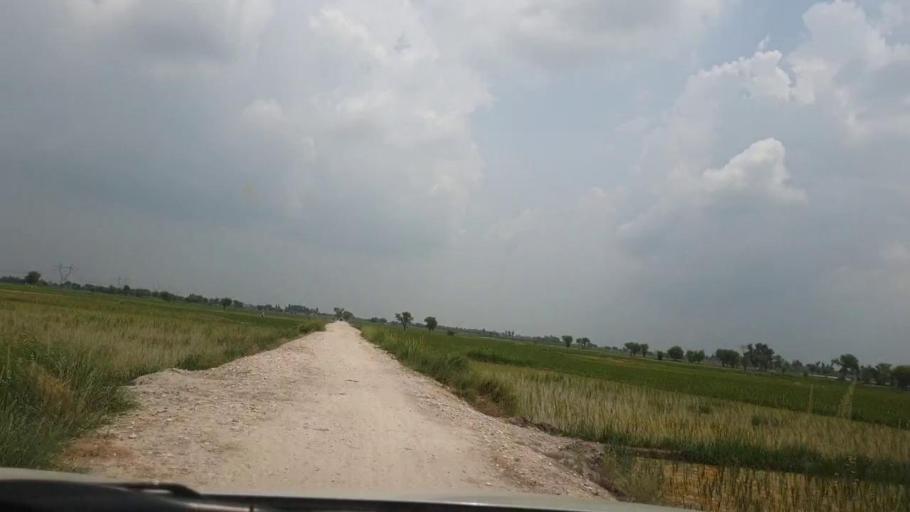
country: PK
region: Sindh
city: Goth Garelo
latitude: 27.4174
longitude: 68.0746
